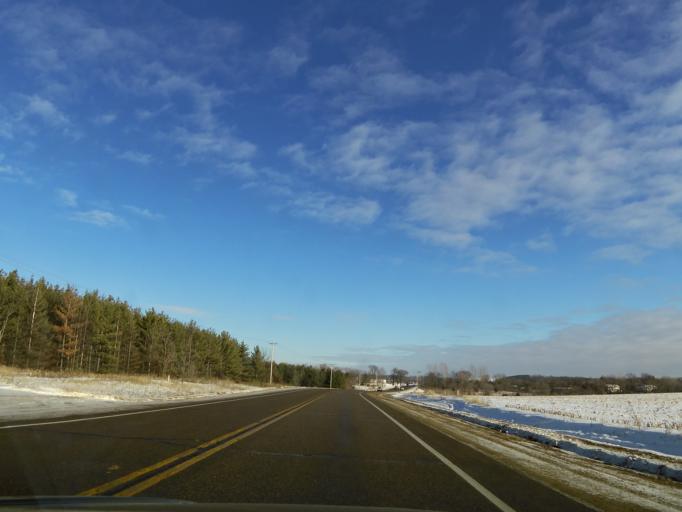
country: US
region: Wisconsin
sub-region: Saint Croix County
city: North Hudson
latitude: 44.9885
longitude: -92.6757
